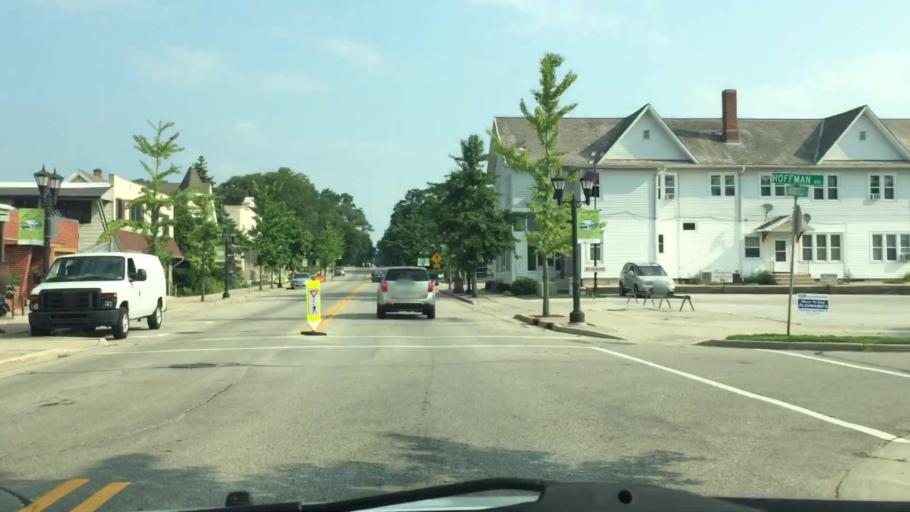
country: US
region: Wisconsin
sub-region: Waukesha County
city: Brookfield
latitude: 43.0723
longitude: -88.1459
